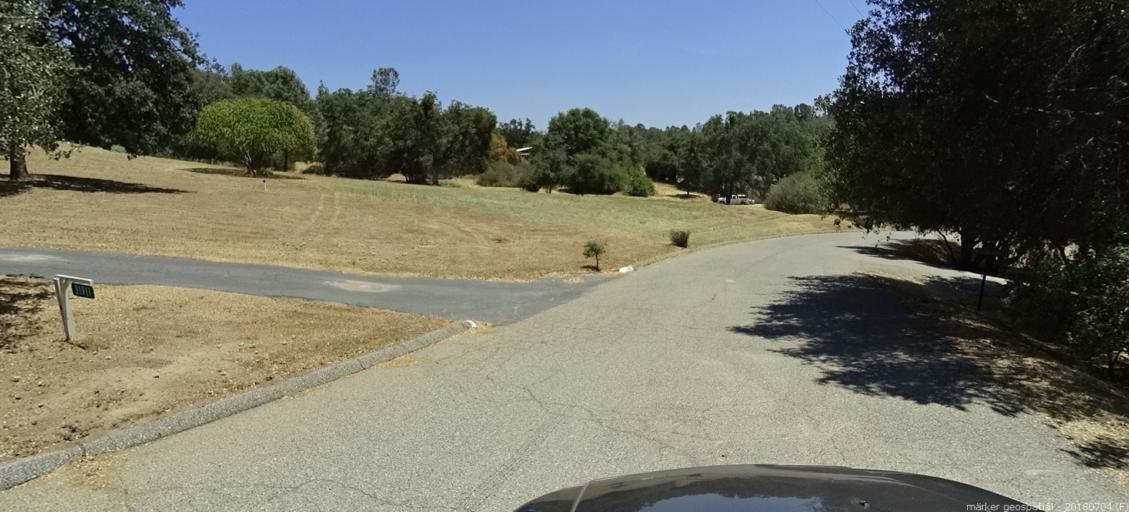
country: US
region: California
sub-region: Madera County
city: Oakhurst
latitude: 37.2118
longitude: -119.5601
